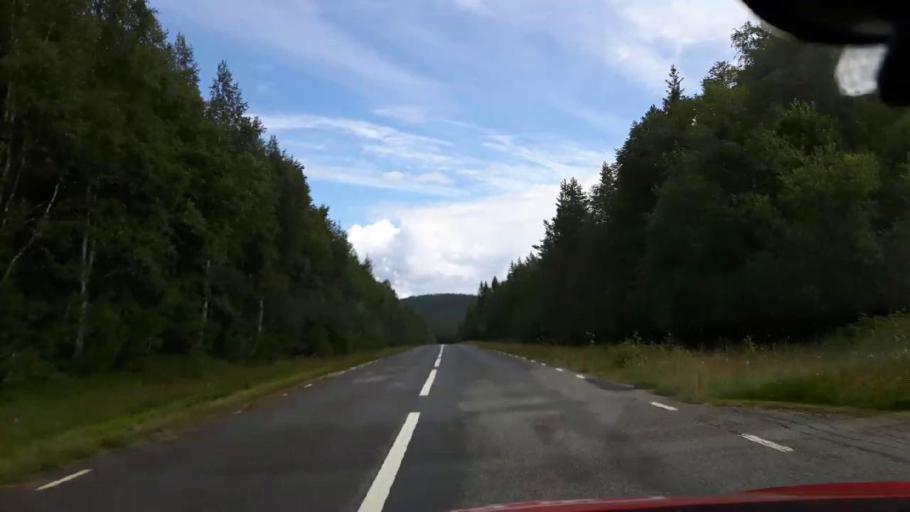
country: SE
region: Jaemtland
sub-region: Stroemsunds Kommun
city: Stroemsund
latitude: 64.3361
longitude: 14.9629
